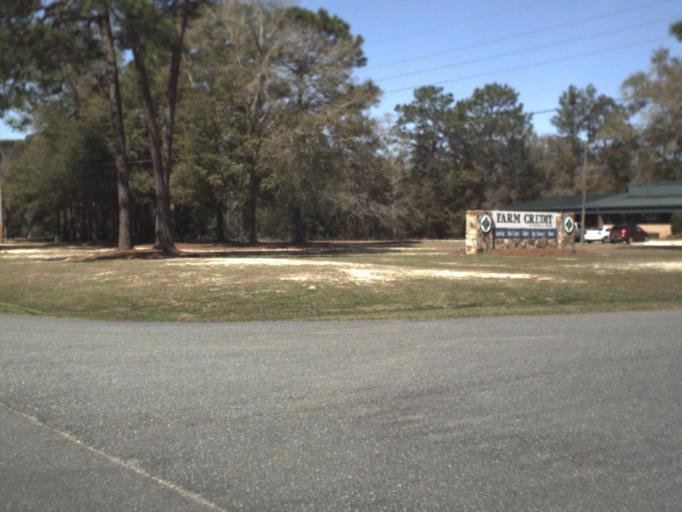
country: US
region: Florida
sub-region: Jackson County
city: Marianna
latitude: 30.7464
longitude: -85.1750
